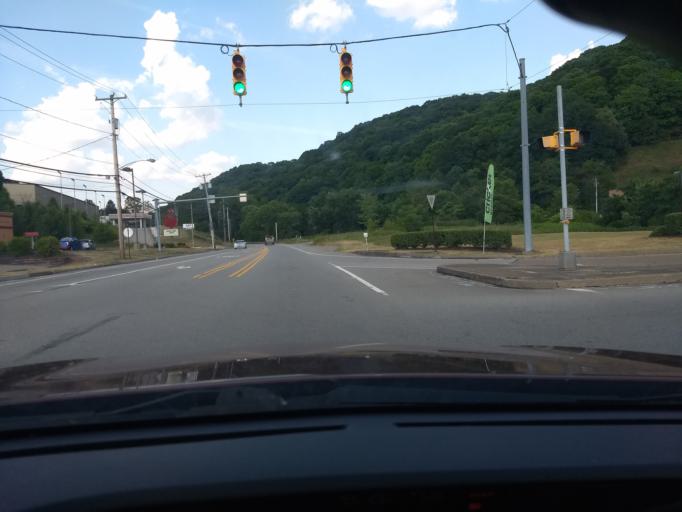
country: US
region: Pennsylvania
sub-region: Allegheny County
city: White Oak
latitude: 40.3381
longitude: -79.8068
